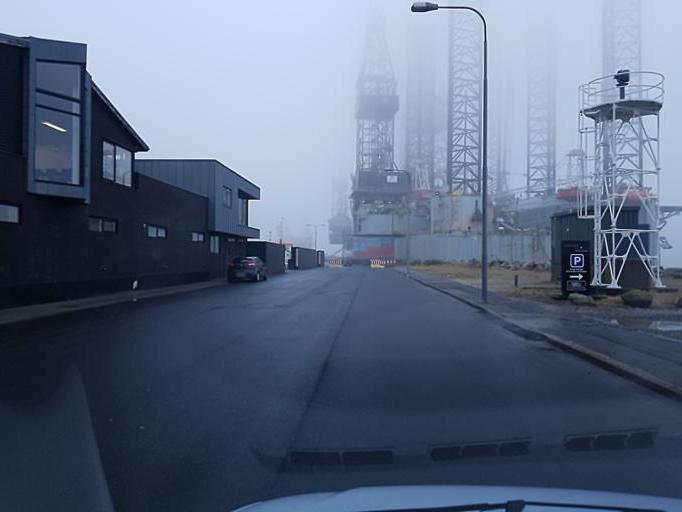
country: DK
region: South Denmark
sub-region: Fano Kommune
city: Nordby
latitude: 55.4787
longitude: 8.4103
